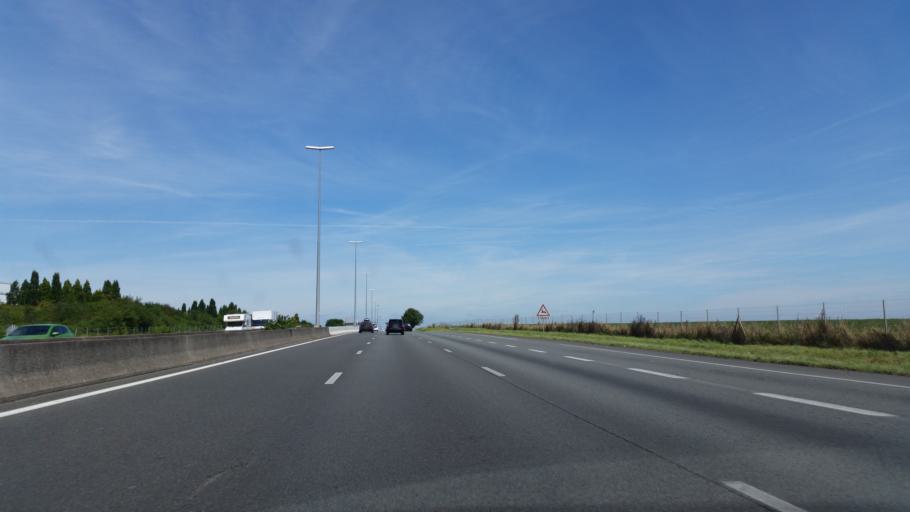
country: FR
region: Nord-Pas-de-Calais
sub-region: Departement du Pas-de-Calais
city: Fampoux
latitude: 50.2737
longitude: 2.8713
